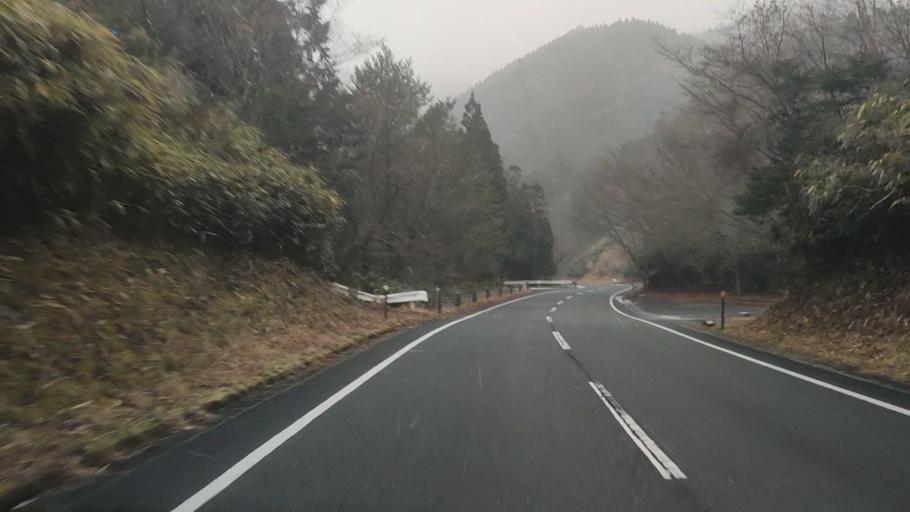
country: JP
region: Kumamoto
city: Matsubase
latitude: 32.5689
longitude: 130.9097
